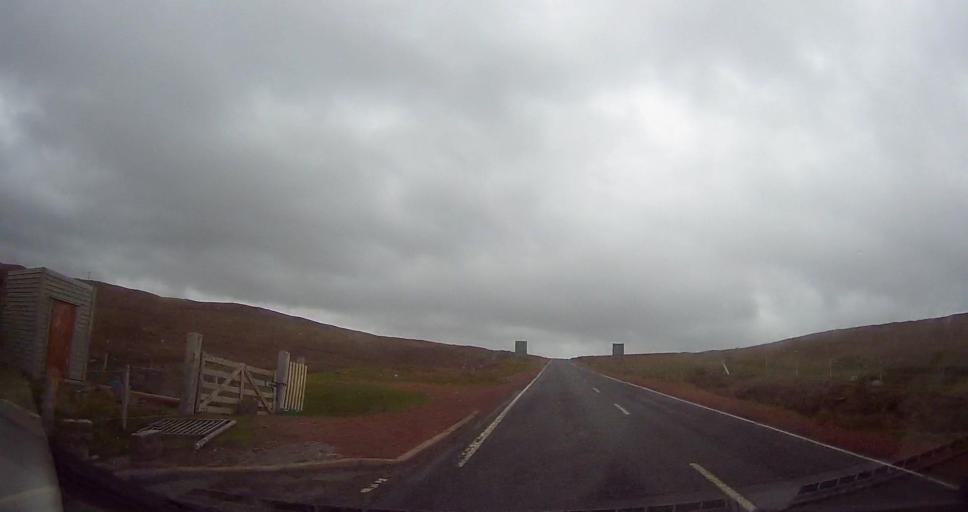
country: GB
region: Scotland
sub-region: Shetland Islands
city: Lerwick
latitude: 60.4867
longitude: -1.4493
